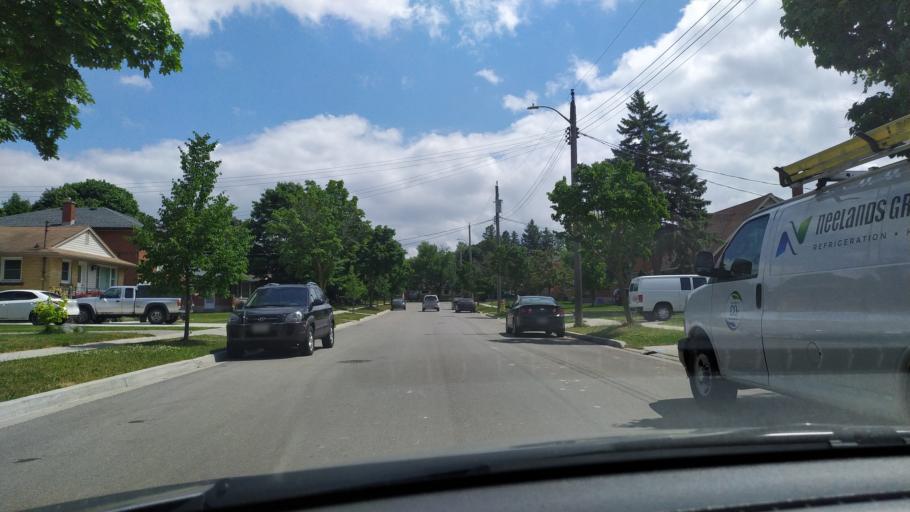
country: CA
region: Ontario
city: Kitchener
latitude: 43.4333
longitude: -80.4840
